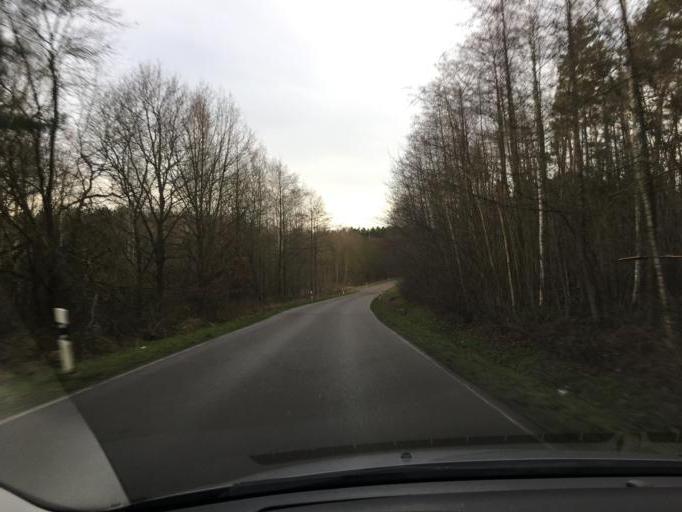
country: DE
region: Saxony
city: Grossposna
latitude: 51.2262
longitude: 12.5037
